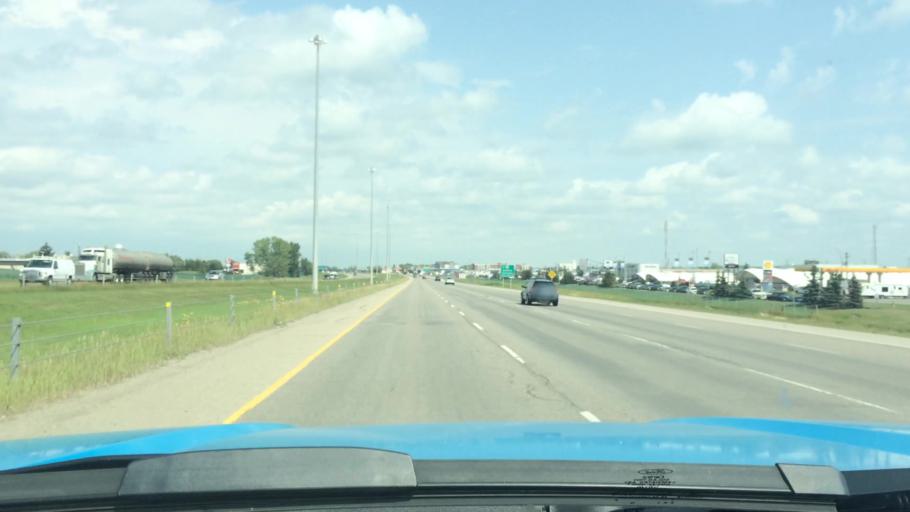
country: CA
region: Alberta
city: Airdrie
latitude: 51.2856
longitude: -114.0007
